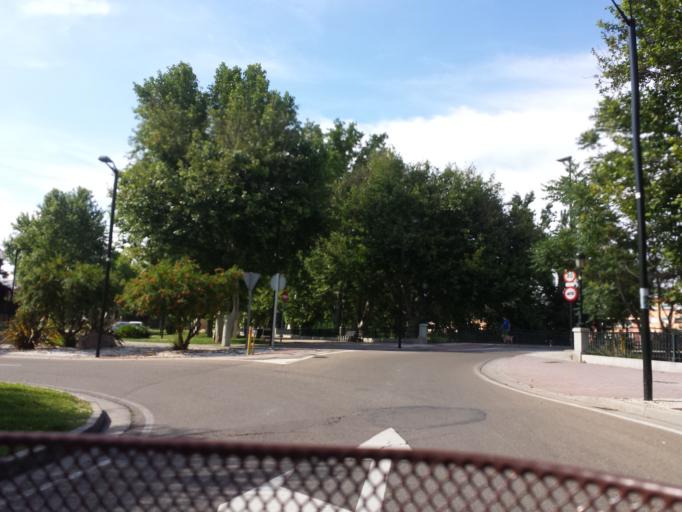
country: ES
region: Aragon
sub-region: Provincia de Zaragoza
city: Delicias
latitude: 41.6294
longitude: -0.9105
